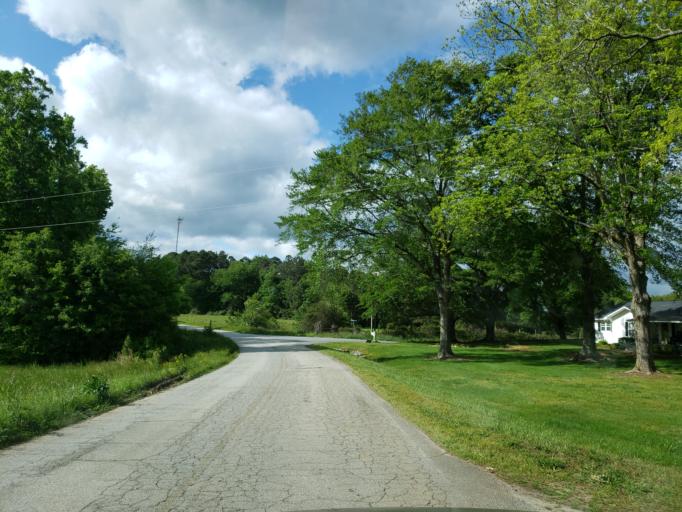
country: US
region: Georgia
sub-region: Haralson County
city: Tallapoosa
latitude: 33.6659
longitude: -85.2837
